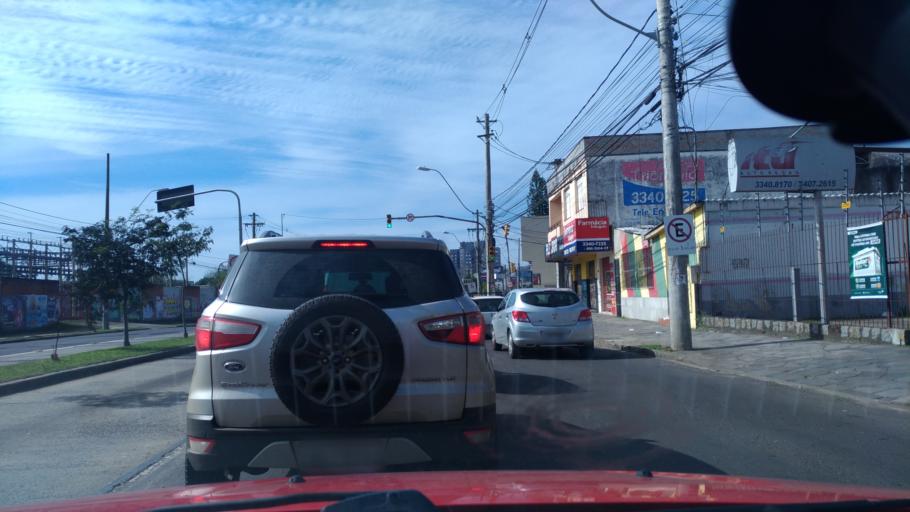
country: BR
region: Rio Grande do Sul
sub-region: Cachoeirinha
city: Cachoeirinha
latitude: -30.0098
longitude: -51.1420
